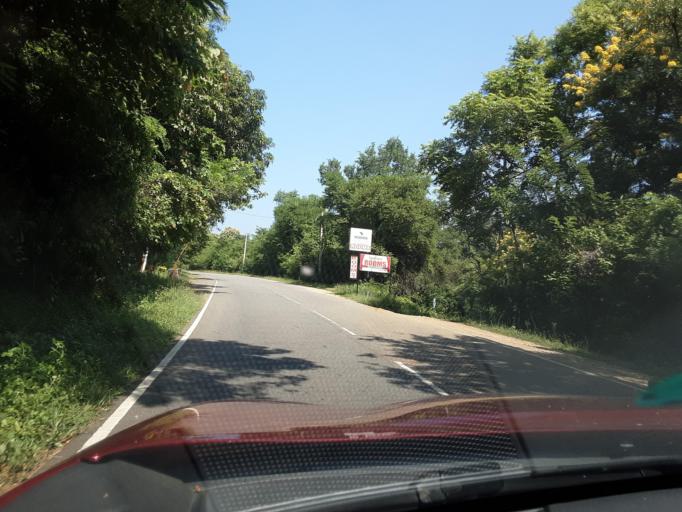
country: LK
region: Uva
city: Badulla
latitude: 7.2708
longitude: 81.0525
